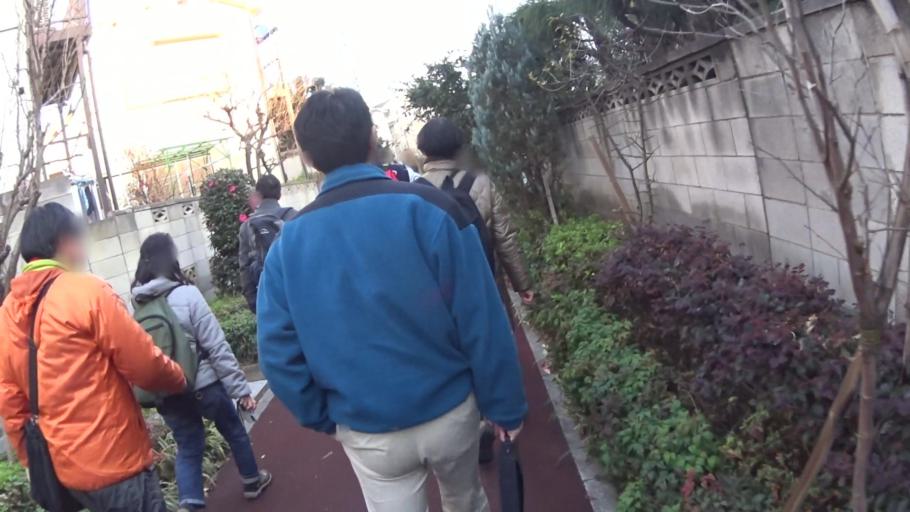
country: JP
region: Saitama
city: Yono
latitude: 35.8673
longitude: 139.6472
